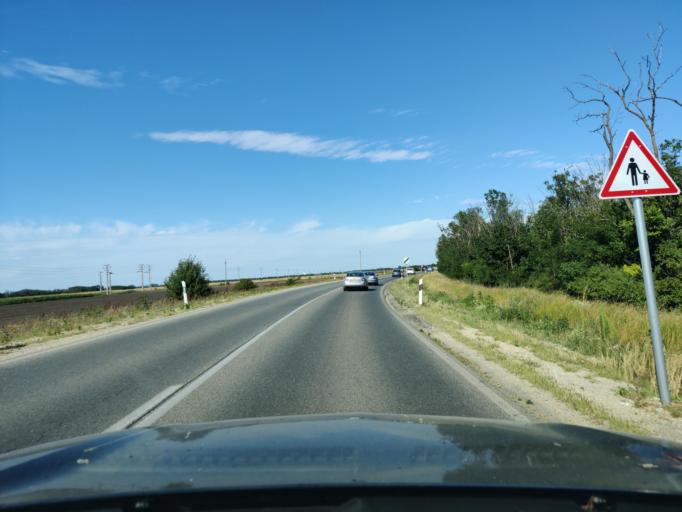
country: HU
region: Gyor-Moson-Sopron
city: Janossomorja
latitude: 47.8130
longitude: 17.1758
